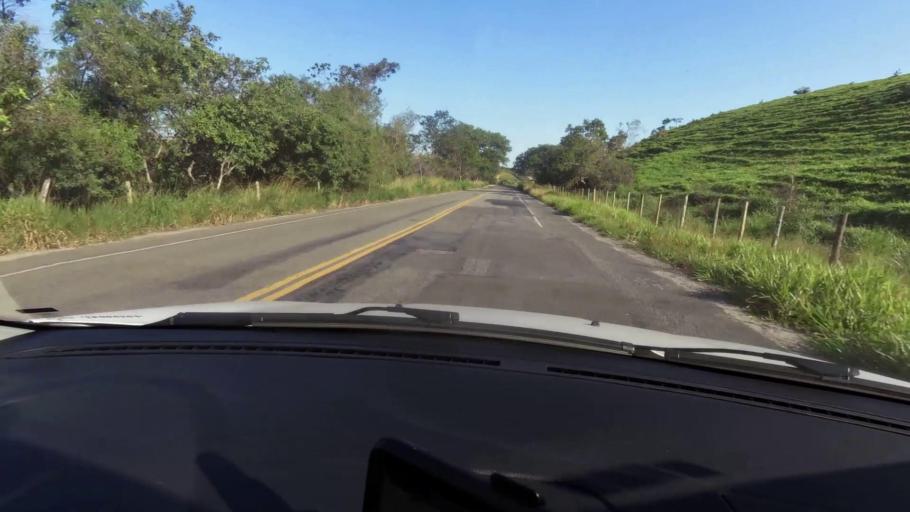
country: BR
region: Espirito Santo
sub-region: Piuma
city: Piuma
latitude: -20.7399
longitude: -40.6475
